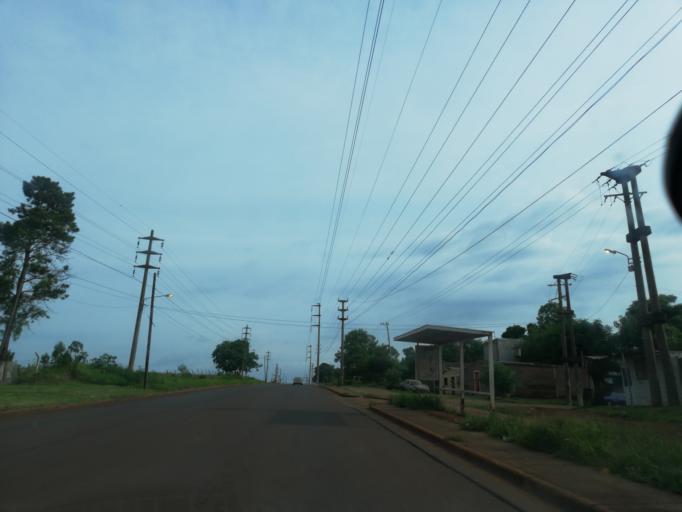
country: AR
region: Misiones
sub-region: Departamento de Capital
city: Posadas
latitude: -27.4315
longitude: -55.9148
